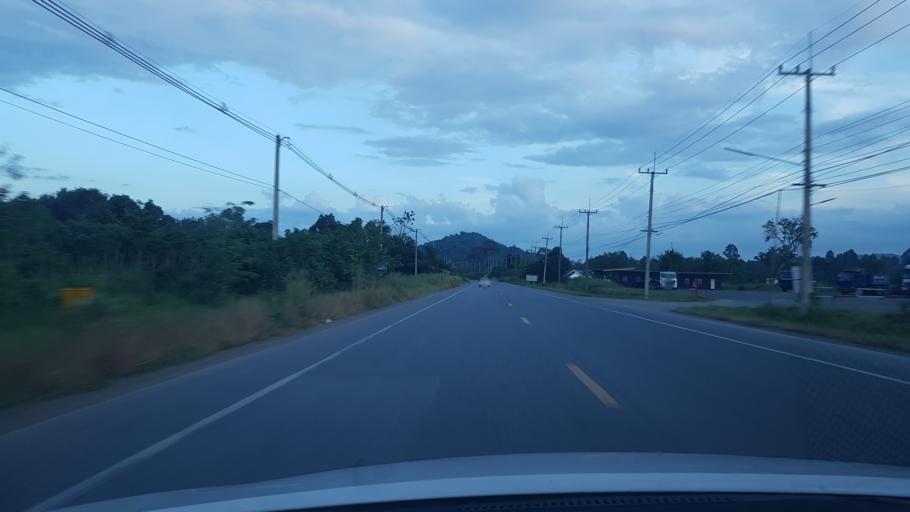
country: TH
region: Sara Buri
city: Kaeng Khoi
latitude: 14.4760
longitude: 101.0595
